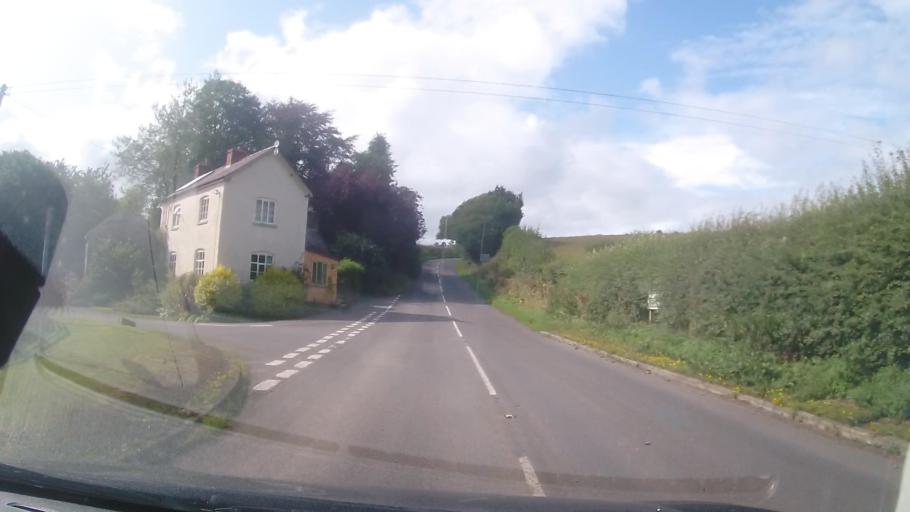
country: GB
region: Wales
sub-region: Sir Powys
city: Knighton
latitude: 52.3842
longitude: -3.0386
